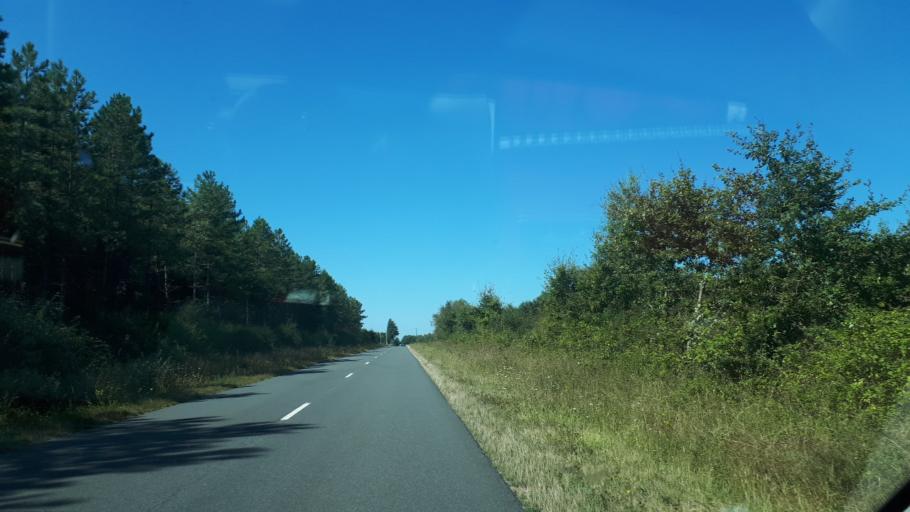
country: FR
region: Centre
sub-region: Departement du Cher
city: Brinon-sur-Sauldre
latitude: 47.6586
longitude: 2.2122
